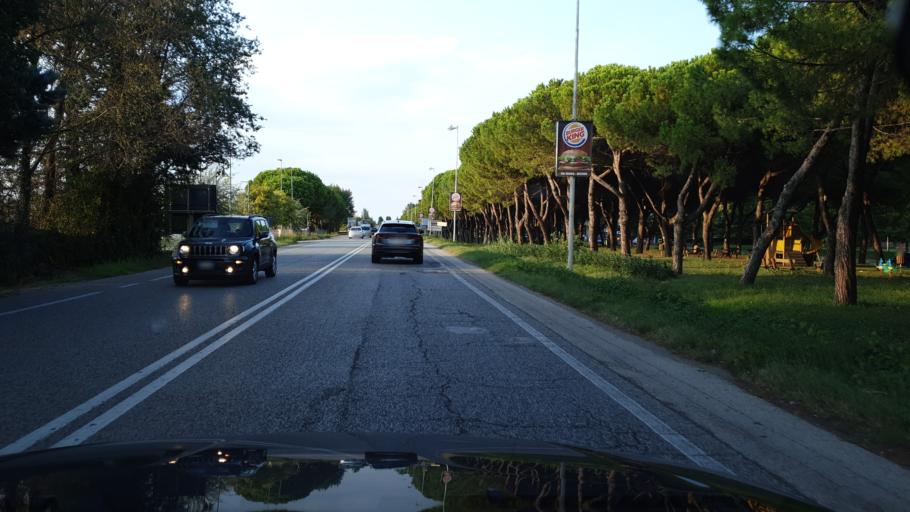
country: IT
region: Emilia-Romagna
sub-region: Provincia di Rimini
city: Riccione
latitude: 44.0064
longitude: 12.6336
